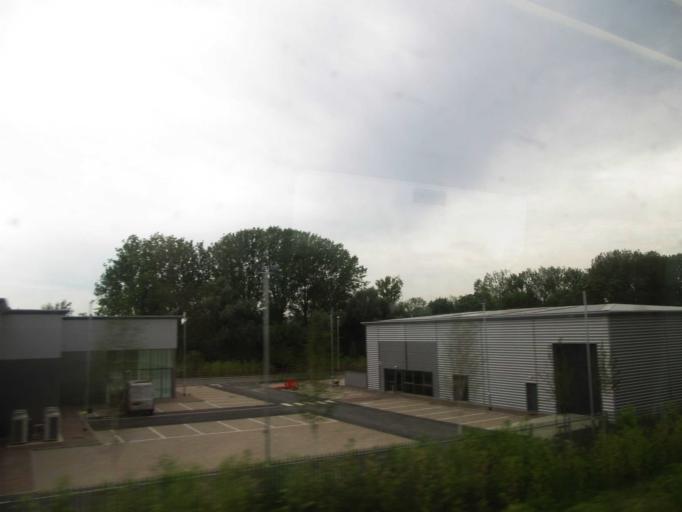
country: GB
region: England
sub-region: Bedford
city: Elstow
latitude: 52.1094
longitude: -0.4798
